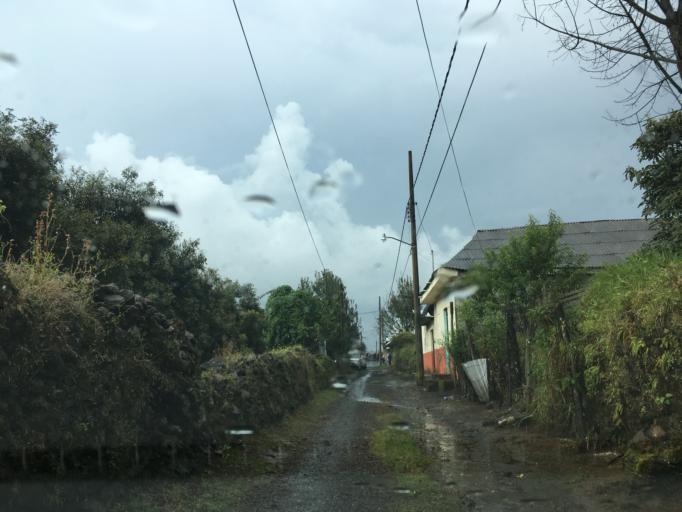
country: MX
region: Michoacan
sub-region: Uruapan
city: Santa Ana Zirosto
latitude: 19.5642
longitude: -102.2854
